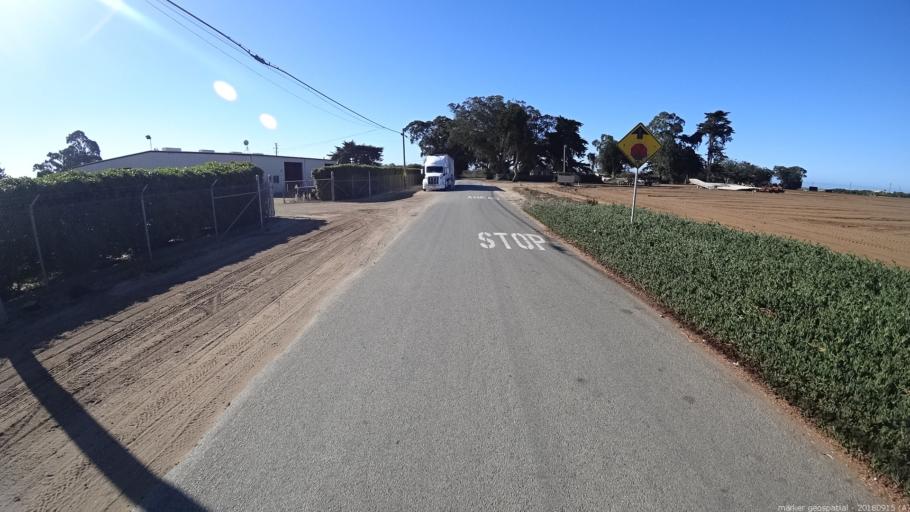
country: US
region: California
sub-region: Monterey County
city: Elkhorn
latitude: 36.8248
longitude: -121.7800
